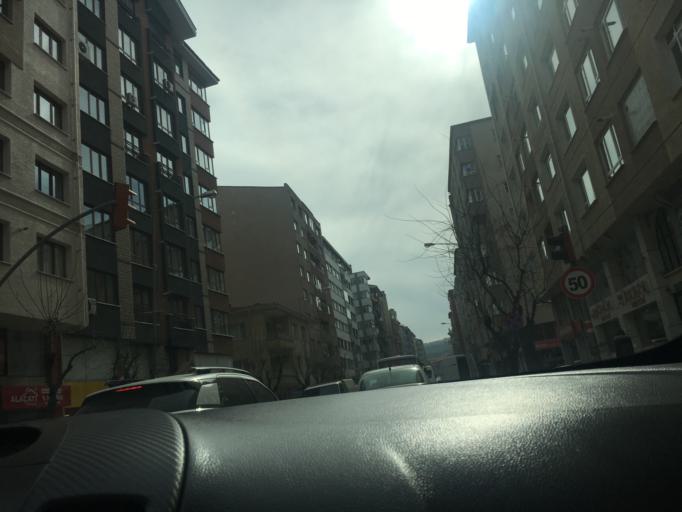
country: TR
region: Eskisehir
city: Eskisehir
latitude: 39.7688
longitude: 30.5176
